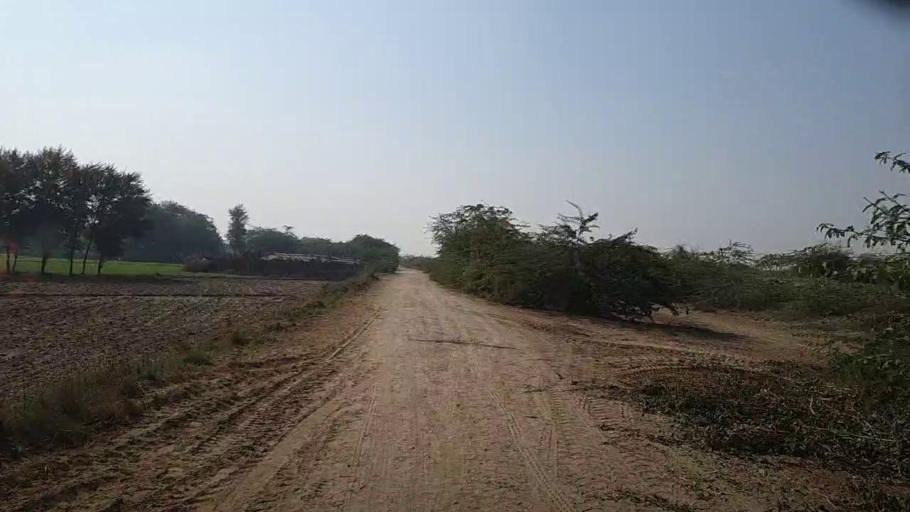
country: PK
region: Sindh
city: Bozdar
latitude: 27.2364
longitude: 68.5977
